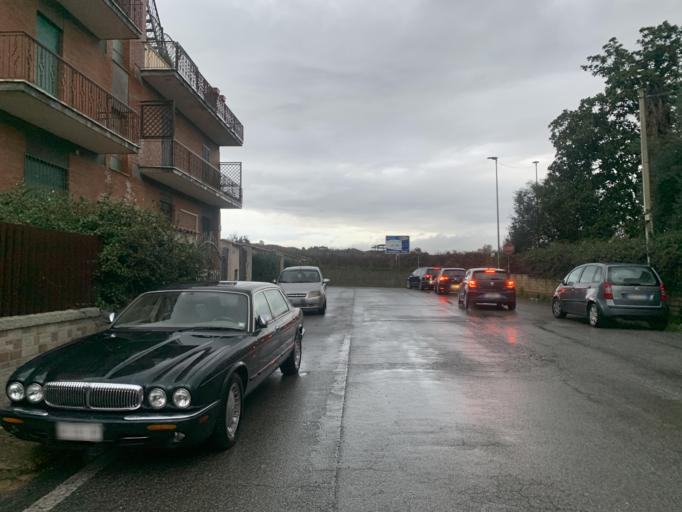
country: IT
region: Latium
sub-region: Citta metropolitana di Roma Capitale
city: Setteville
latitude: 41.9450
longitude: 12.6522
